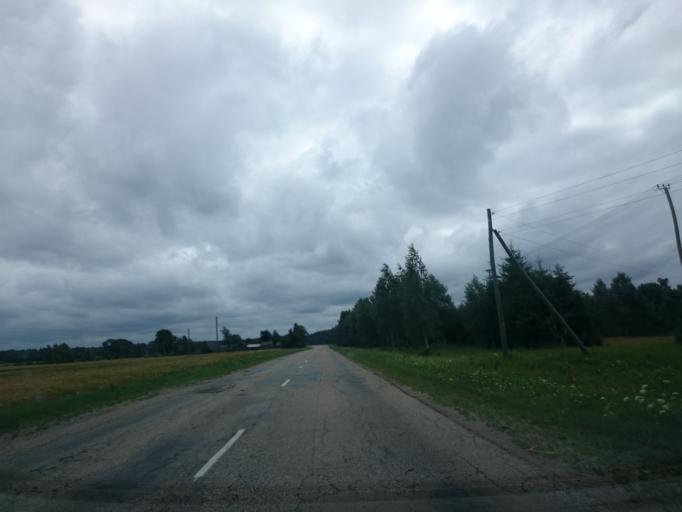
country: LV
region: Pavilostas
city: Pavilosta
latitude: 56.8174
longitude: 21.2273
